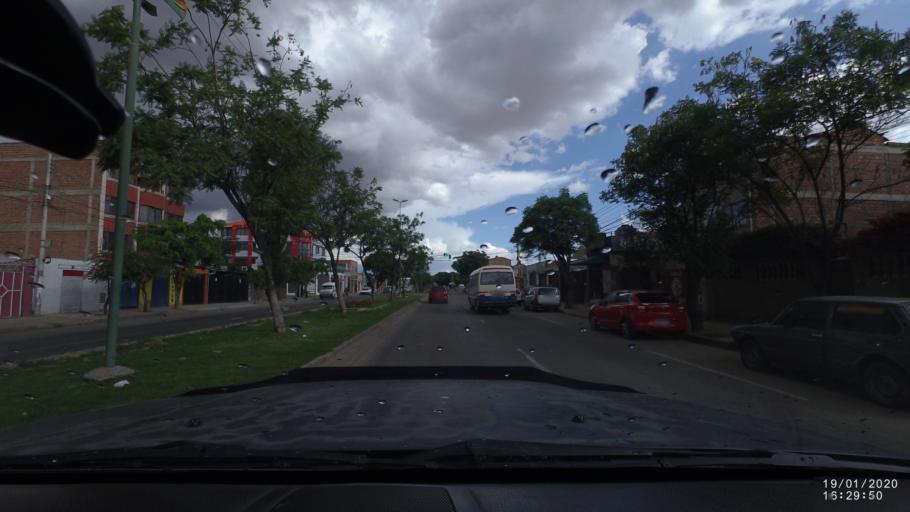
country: BO
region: Cochabamba
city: Cochabamba
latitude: -17.4033
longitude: -66.1817
